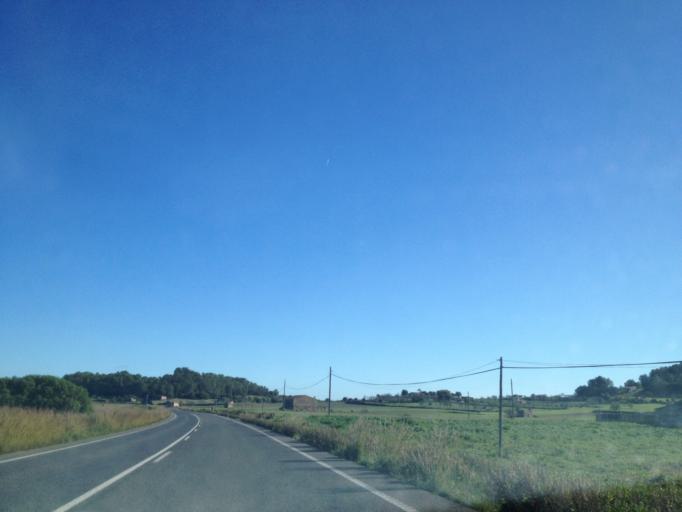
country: ES
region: Balearic Islands
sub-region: Illes Balears
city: Sineu
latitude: 39.6434
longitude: 3.0332
